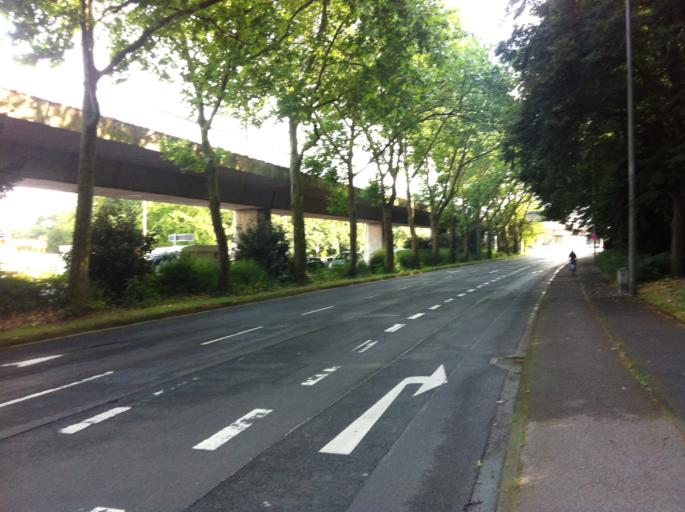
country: DE
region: North Rhine-Westphalia
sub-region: Regierungsbezirk Koln
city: Neuehrenfeld
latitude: 50.9613
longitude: 6.9304
